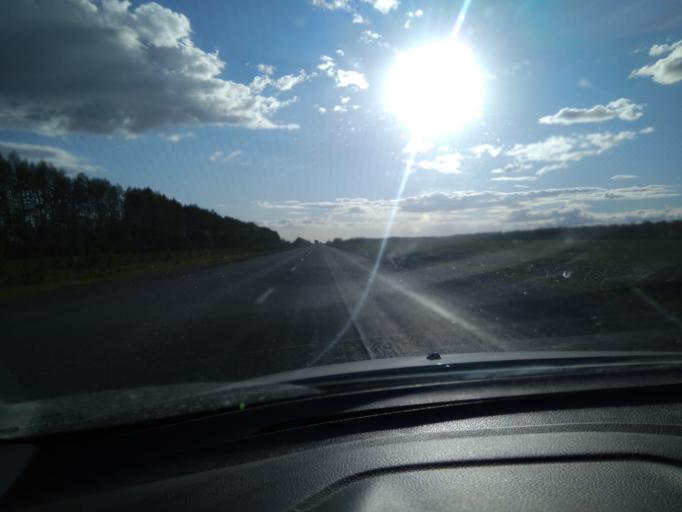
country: RU
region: Sverdlovsk
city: Troitskiy
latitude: 57.0865
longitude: 63.7255
